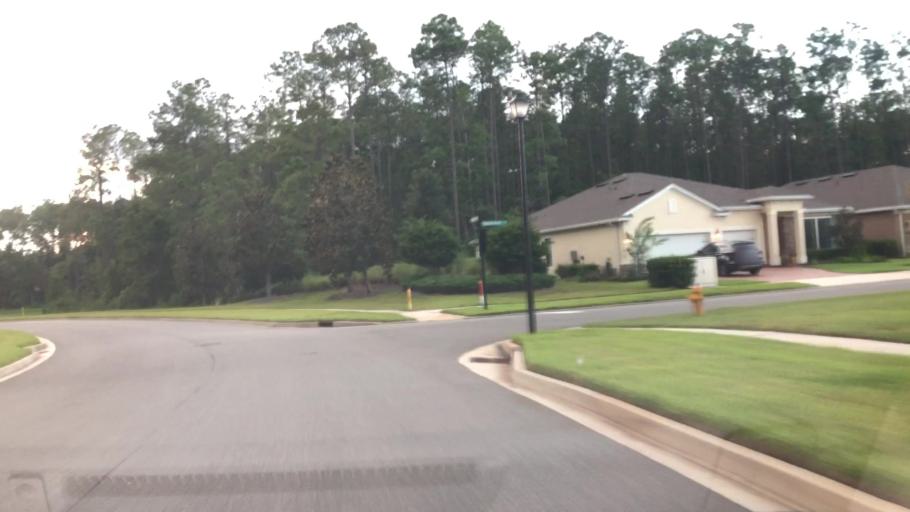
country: US
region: Florida
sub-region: Saint Johns County
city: Palm Valley
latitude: 30.1156
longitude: -81.4512
